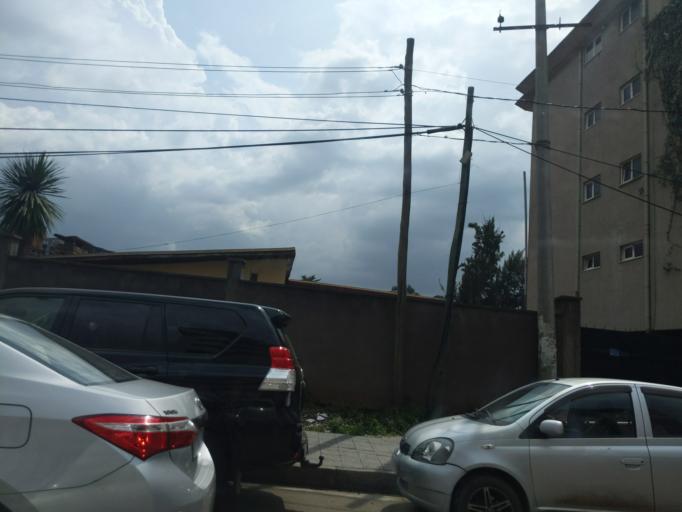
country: ET
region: Adis Abeba
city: Addis Ababa
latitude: 8.9946
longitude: 38.7784
